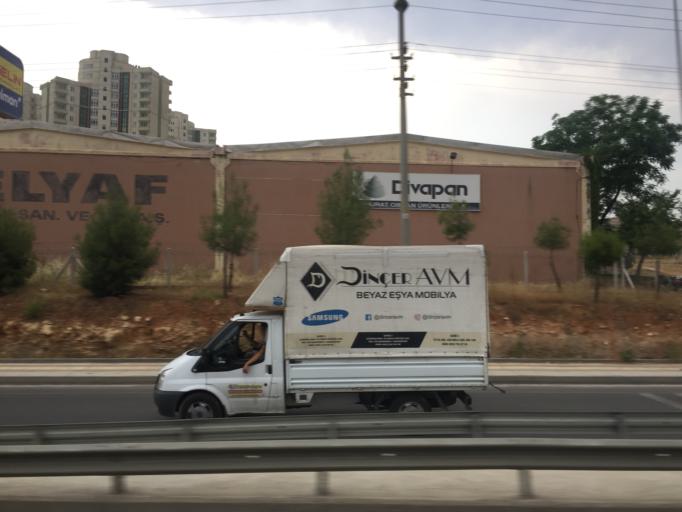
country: TR
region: Gaziantep
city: Gaziantep
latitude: 37.0392
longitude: 37.4238
